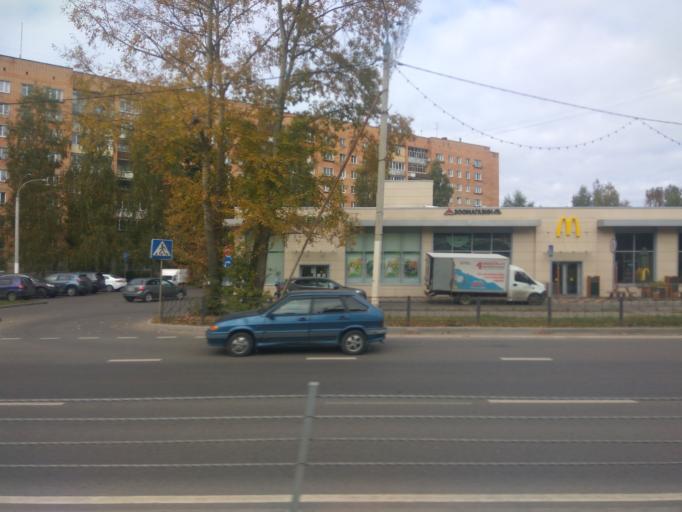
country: RU
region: Moskovskaya
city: Fryazino
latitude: 55.9497
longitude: 38.0482
